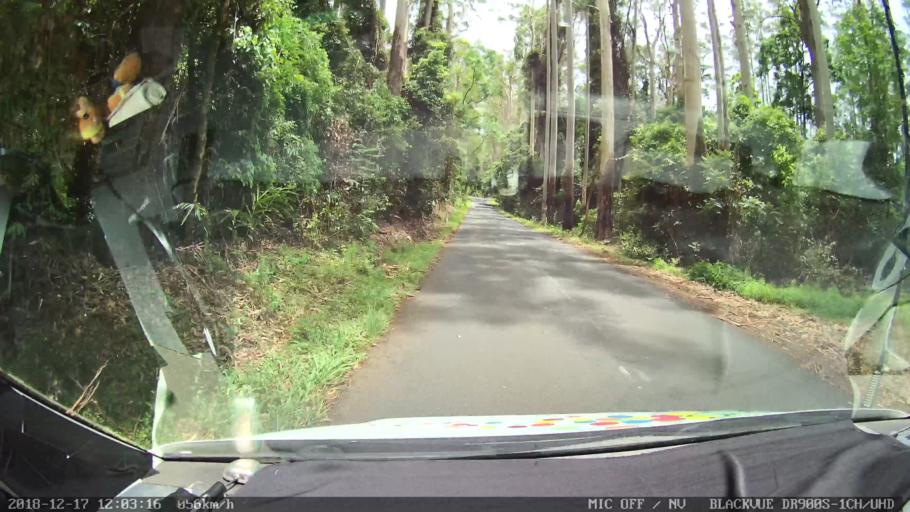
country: AU
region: New South Wales
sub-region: Kyogle
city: Kyogle
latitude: -28.5097
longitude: 152.5684
